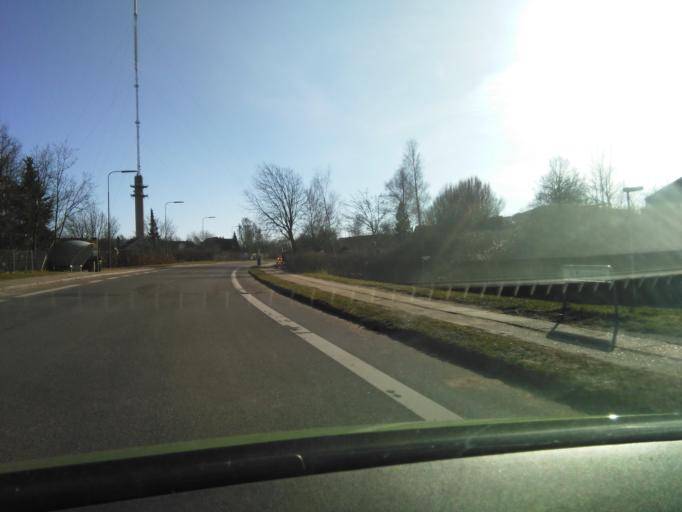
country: DK
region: Central Jutland
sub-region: Arhus Kommune
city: Beder
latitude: 56.1033
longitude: 10.2165
